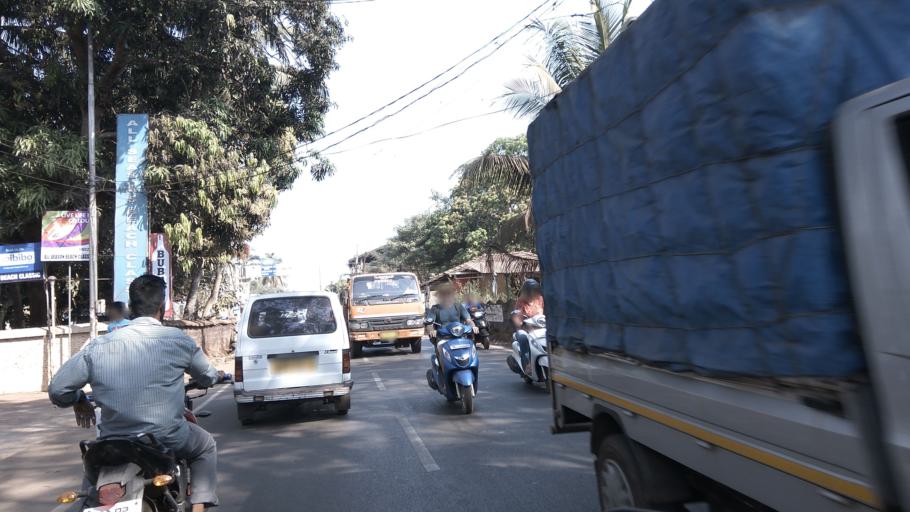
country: IN
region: Goa
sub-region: North Goa
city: Candolim
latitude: 15.5304
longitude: 73.7646
